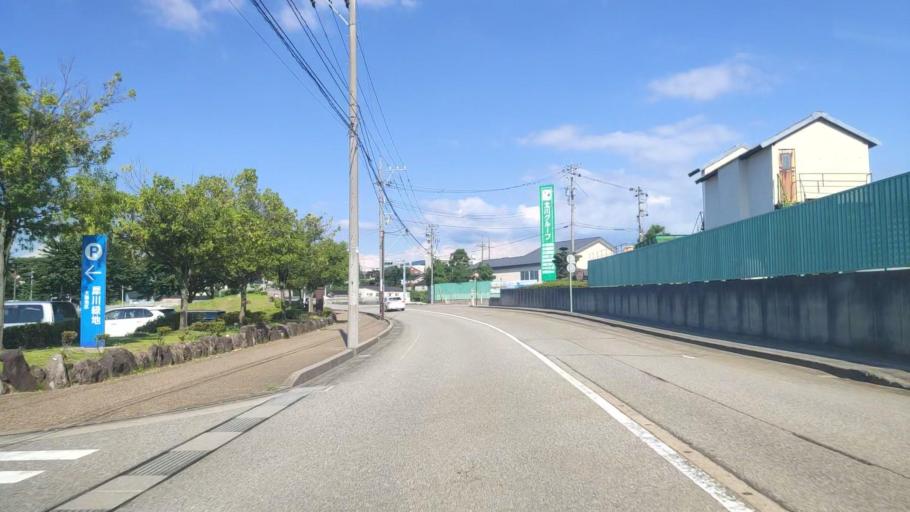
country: JP
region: Ishikawa
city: Nonoichi
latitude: 36.5383
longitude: 136.6766
